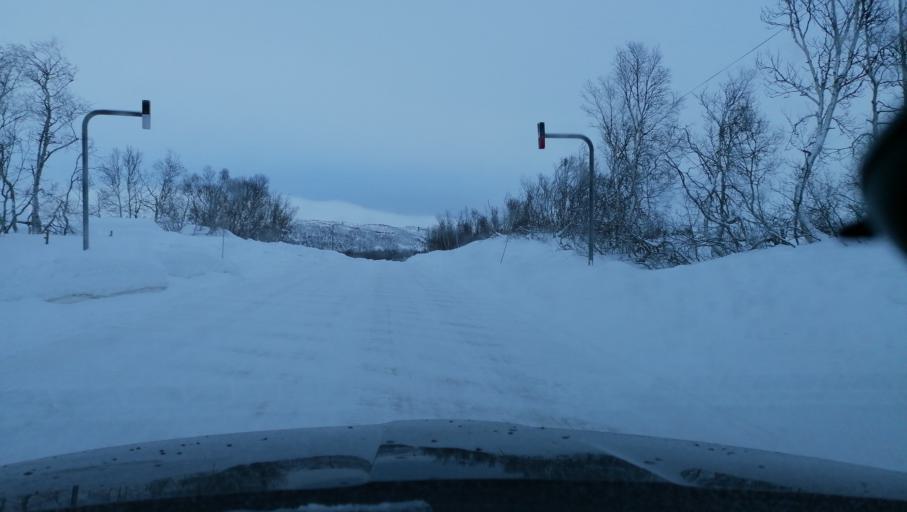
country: NO
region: Aust-Agder
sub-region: Bykle
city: Hovden
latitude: 59.6425
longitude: 7.4579
